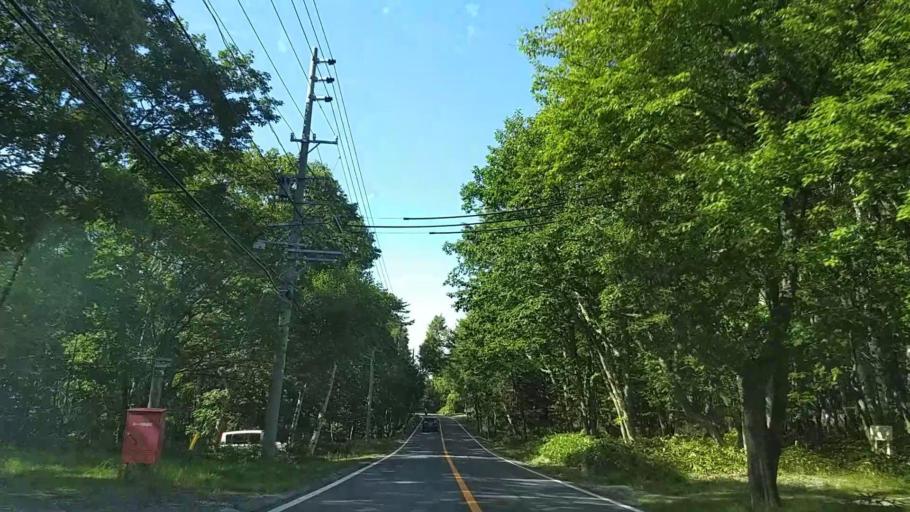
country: JP
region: Nagano
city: Chino
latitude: 36.1042
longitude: 138.2465
